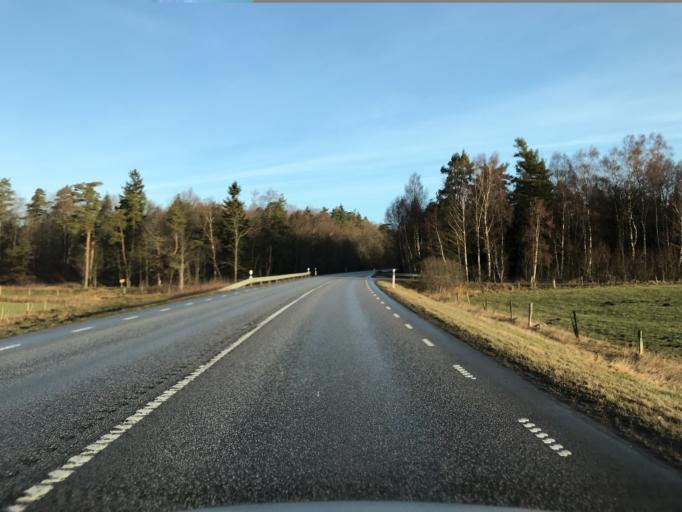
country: SE
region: Skane
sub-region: Hassleholms Kommun
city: Bjarnum
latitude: 56.2590
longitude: 13.7178
